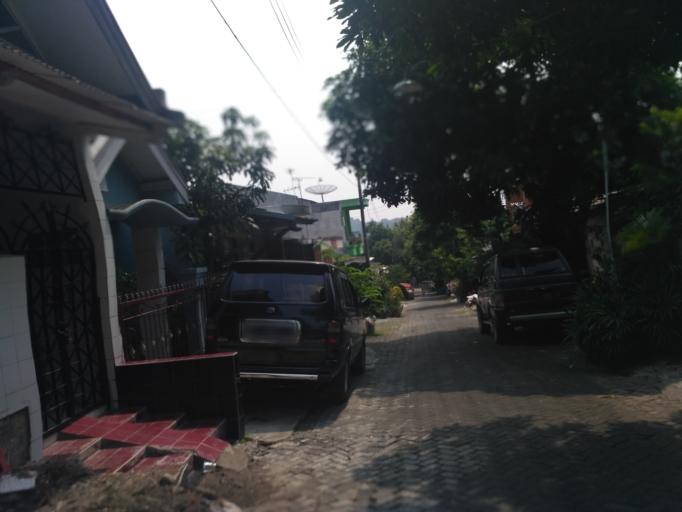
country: ID
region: Central Java
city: Mranggen
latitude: -7.0651
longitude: 110.4597
